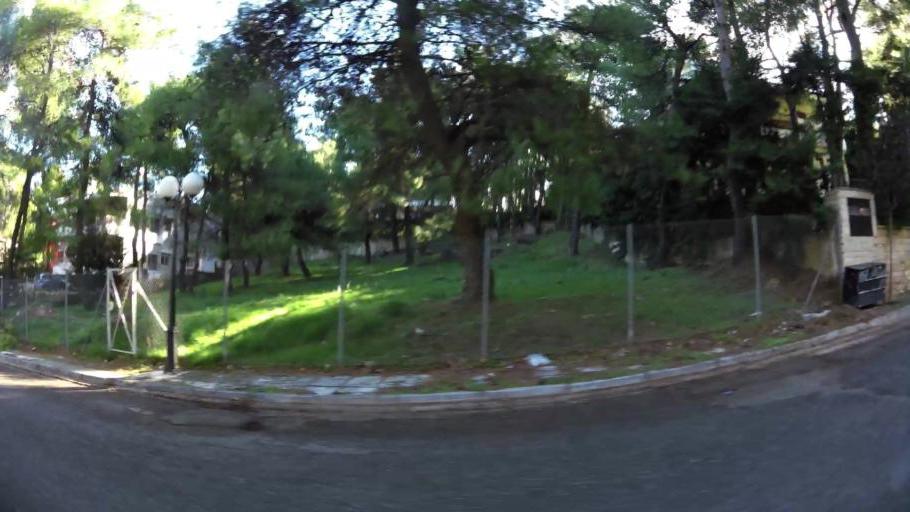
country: GR
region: Attica
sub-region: Nomarchia Anatolikis Attikis
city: Stamata
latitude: 38.1321
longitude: 23.8733
